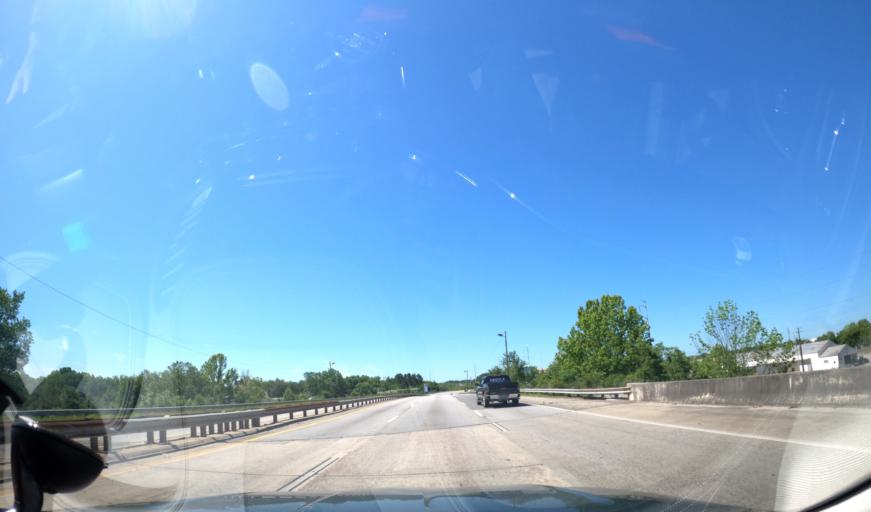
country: US
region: Georgia
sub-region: Richmond County
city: Augusta
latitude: 33.4467
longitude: -81.9772
